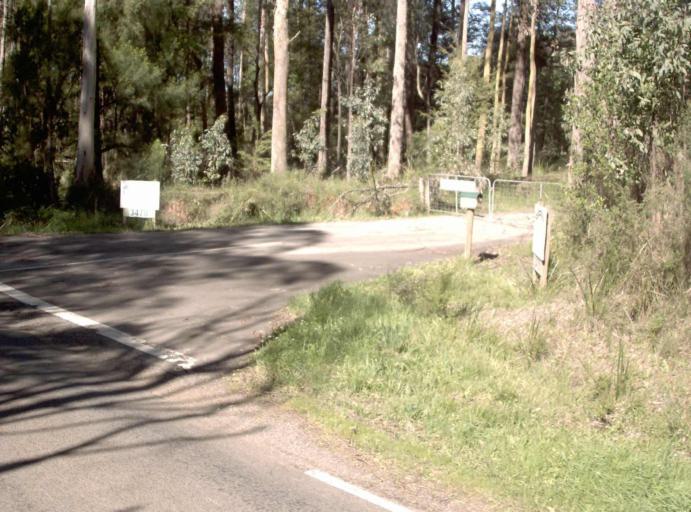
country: AU
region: Victoria
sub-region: Baw Baw
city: Warragul
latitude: -37.8927
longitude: 145.9264
